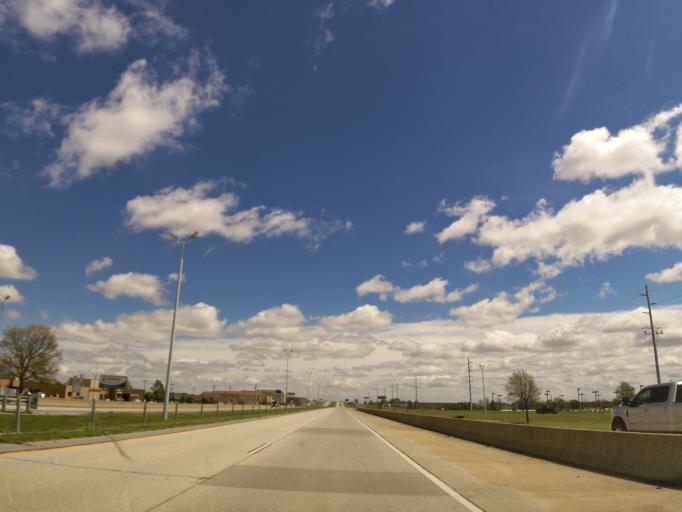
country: US
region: Arkansas
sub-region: Craighead County
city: Jonesboro
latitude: 35.8070
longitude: -90.6685
